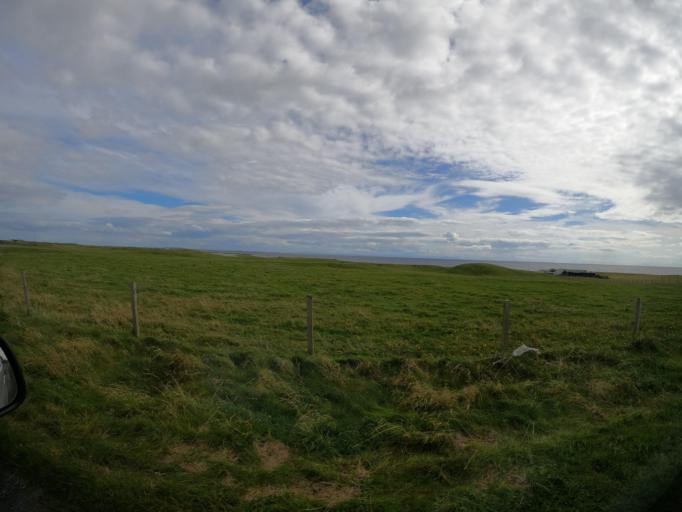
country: GB
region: Scotland
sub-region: Eilean Siar
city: Barra
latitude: 56.4751
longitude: -6.8994
